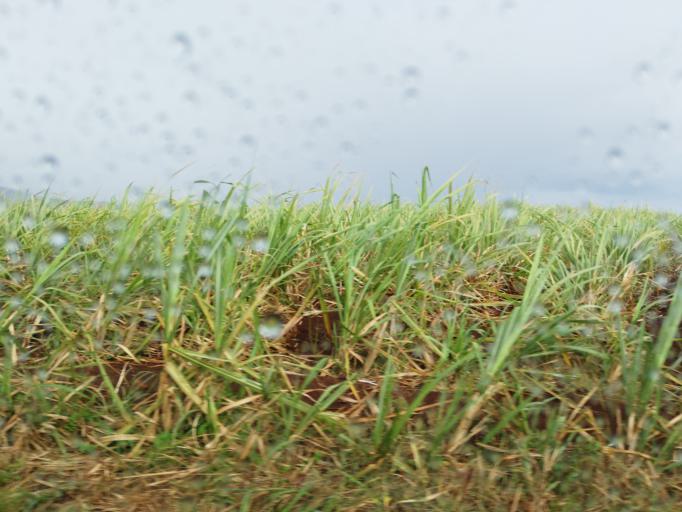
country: MU
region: Pamplemousses
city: Long Mountain
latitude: -20.1277
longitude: 57.5661
